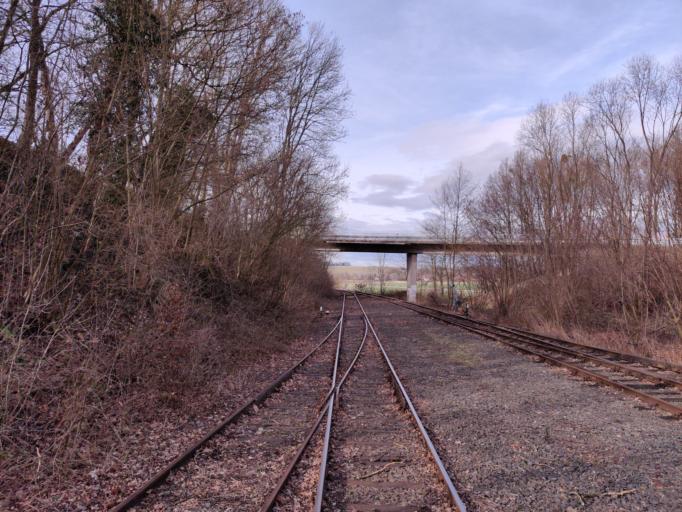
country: DE
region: Lower Saxony
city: Bockenem
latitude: 51.9755
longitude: 10.1289
